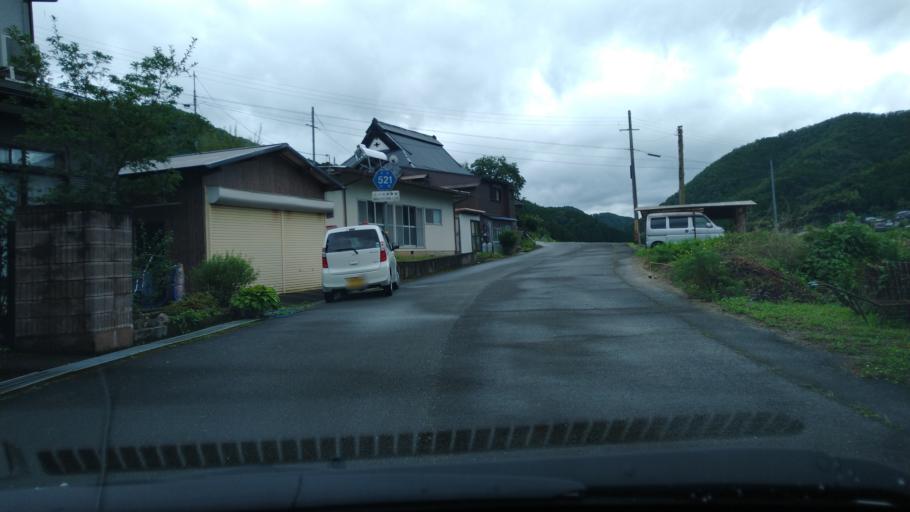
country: JP
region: Kyoto
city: Ayabe
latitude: 35.2422
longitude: 135.2615
